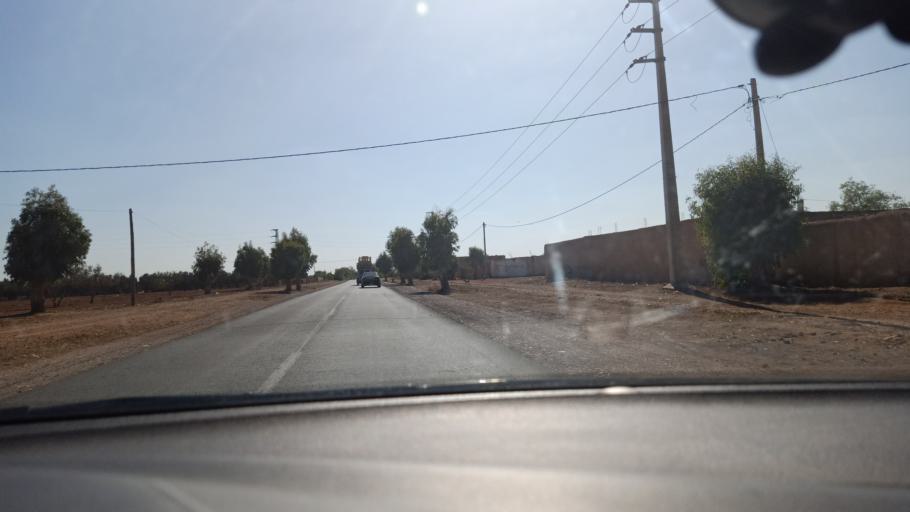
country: MA
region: Doukkala-Abda
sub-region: Safi
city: Youssoufia
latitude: 32.0944
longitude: -8.6156
